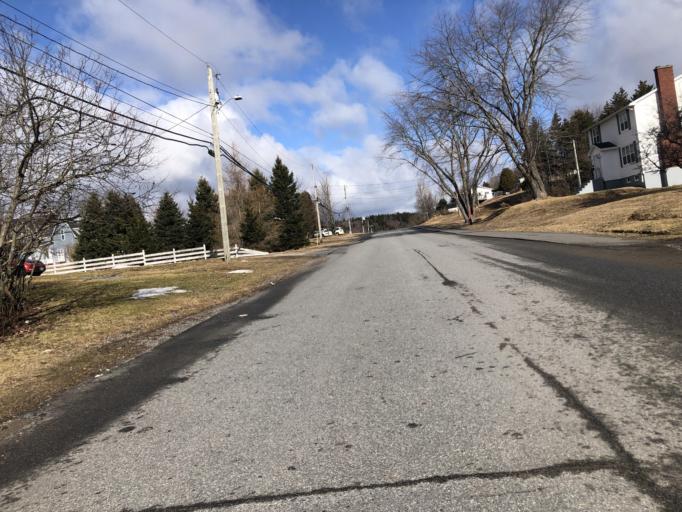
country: CA
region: New Brunswick
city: Saint John
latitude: 45.3188
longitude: -66.0086
